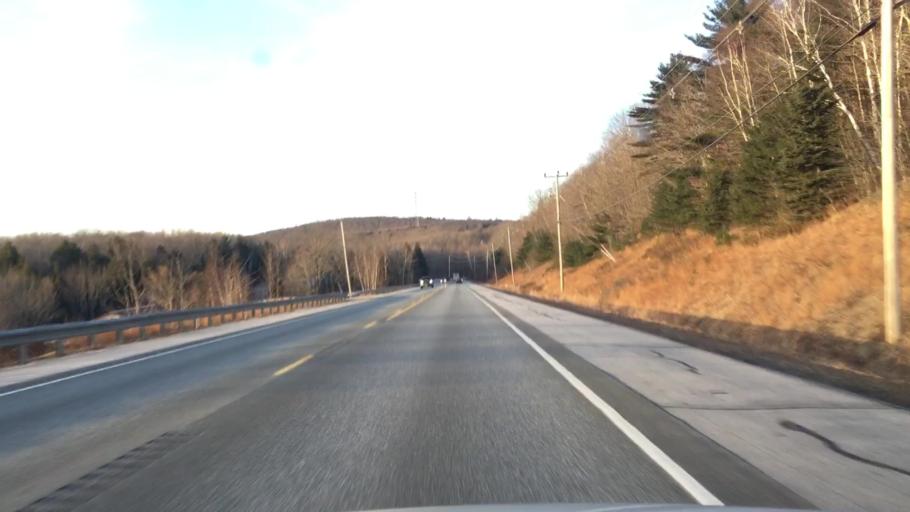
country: US
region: Maine
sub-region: Hancock County
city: Dedham
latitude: 44.7119
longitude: -68.6035
